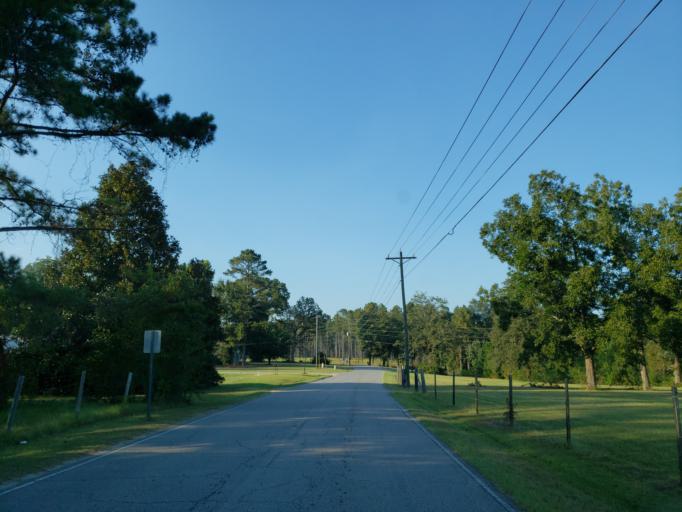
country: US
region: Mississippi
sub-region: Lamar County
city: West Hattiesburg
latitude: 31.3341
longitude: -89.4464
